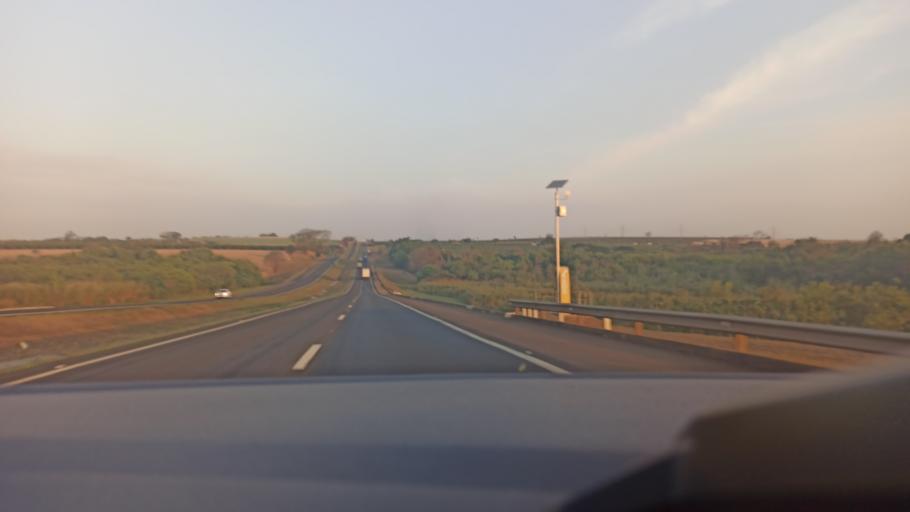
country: BR
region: Sao Paulo
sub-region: Santa Adelia
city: Santa Adelia
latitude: -21.3924
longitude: -48.7188
